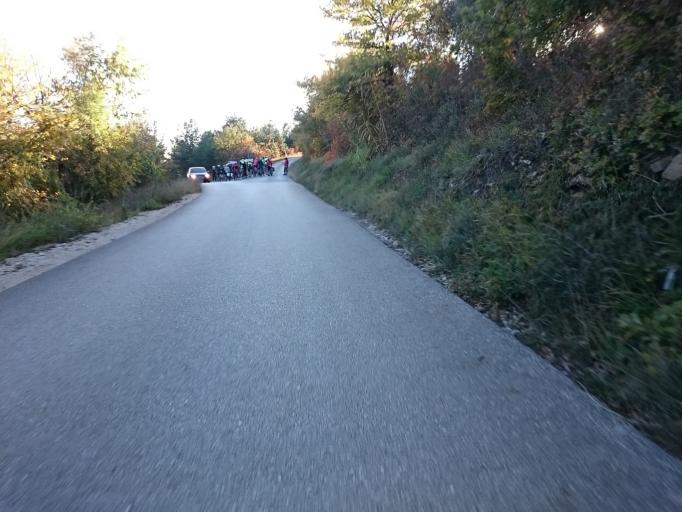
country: HR
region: Istarska
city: Buje
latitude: 45.3816
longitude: 13.7104
